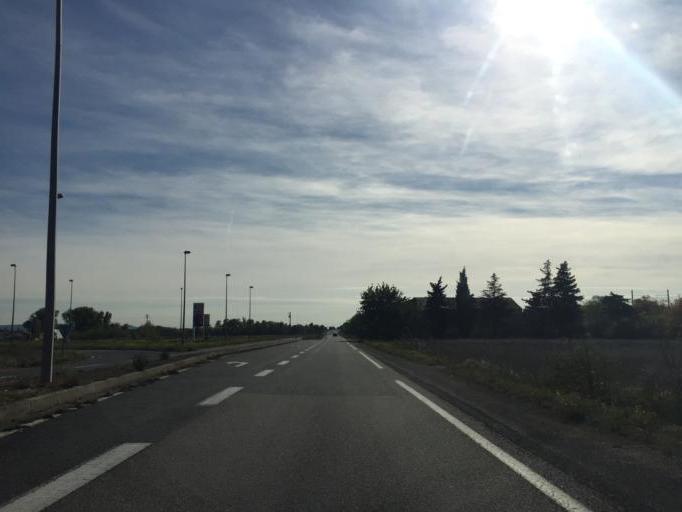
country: FR
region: Rhone-Alpes
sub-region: Departement de la Drome
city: Donzere
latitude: 44.4212
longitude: 4.7116
